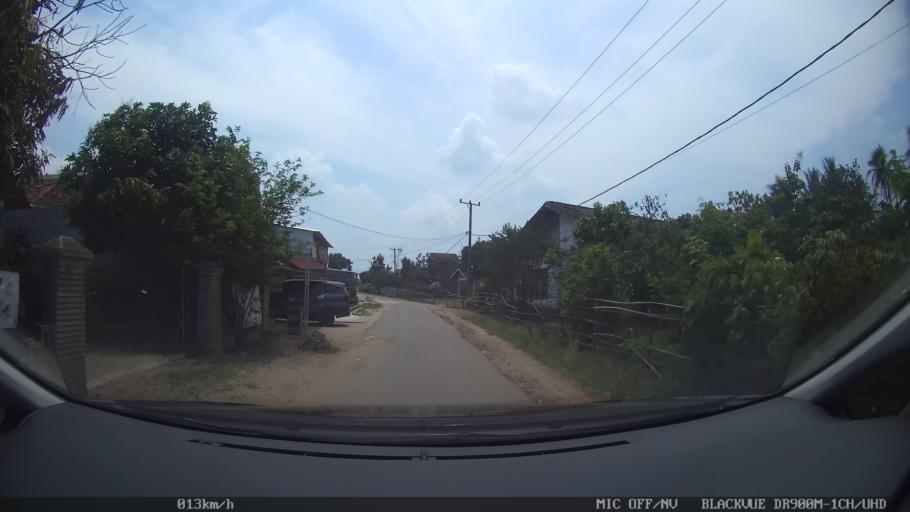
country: ID
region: Lampung
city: Natar
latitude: -5.3132
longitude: 105.2227
